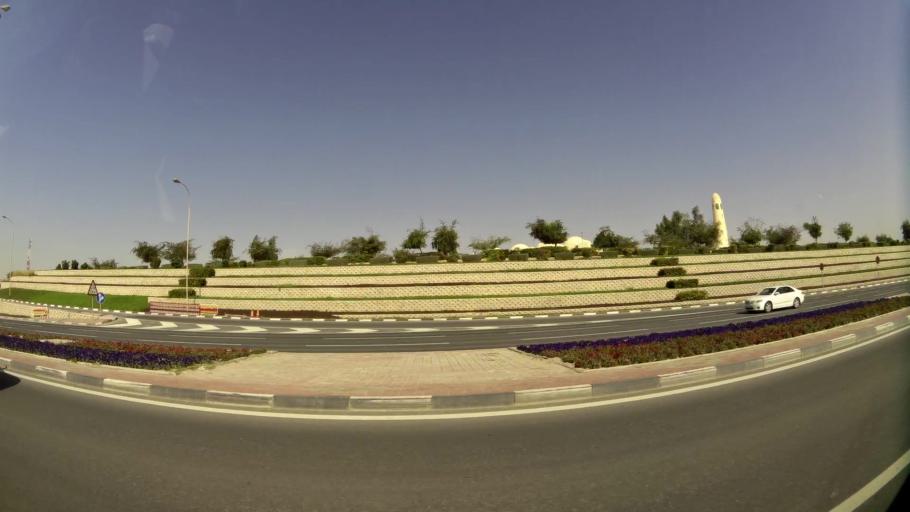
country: QA
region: Baladiyat ad Dawhah
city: Doha
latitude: 25.3150
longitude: 51.5065
